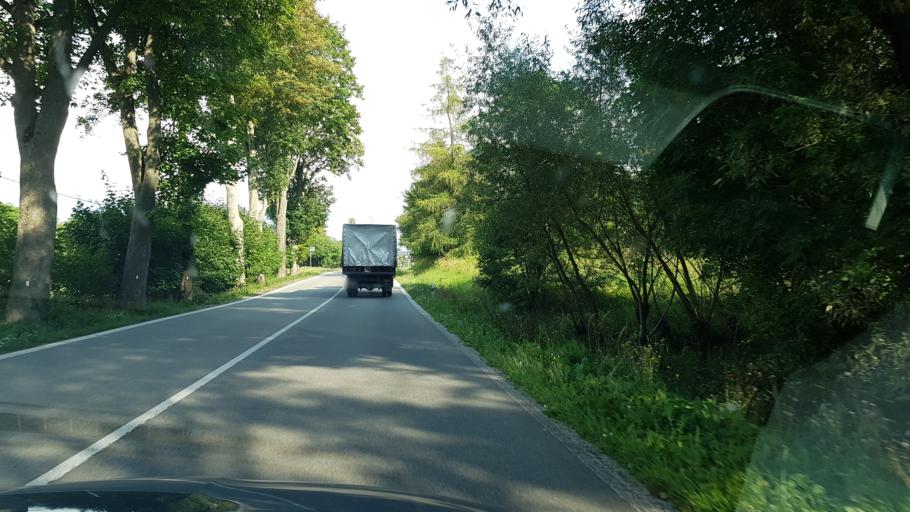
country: CZ
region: Pardubicky
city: Jablonne nad Orlici
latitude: 50.0902
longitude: 16.5939
